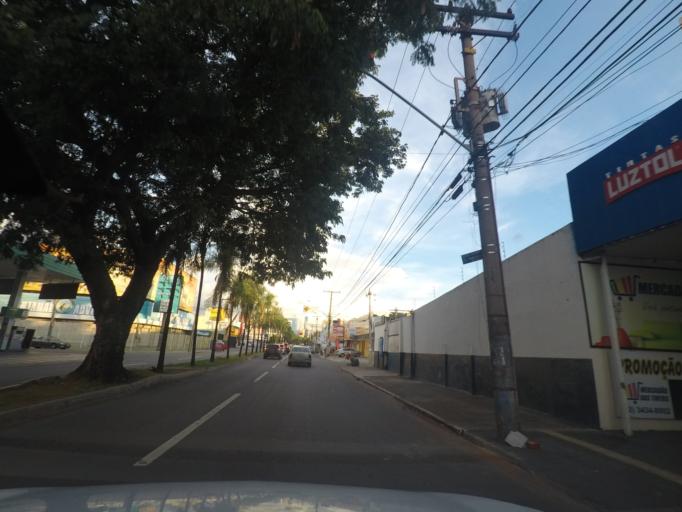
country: BR
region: Goias
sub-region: Goiania
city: Goiania
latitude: -16.6804
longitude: -49.2842
